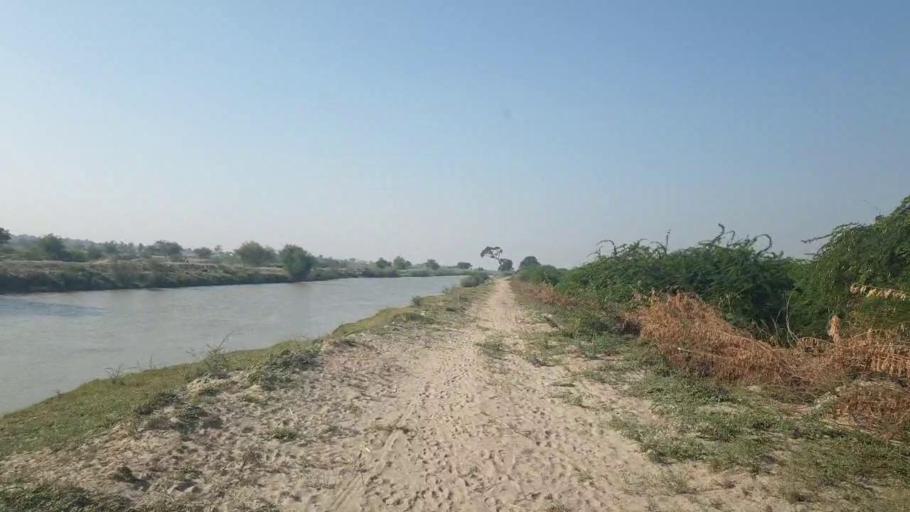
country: PK
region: Sindh
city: Badin
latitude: 24.7003
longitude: 68.8792
